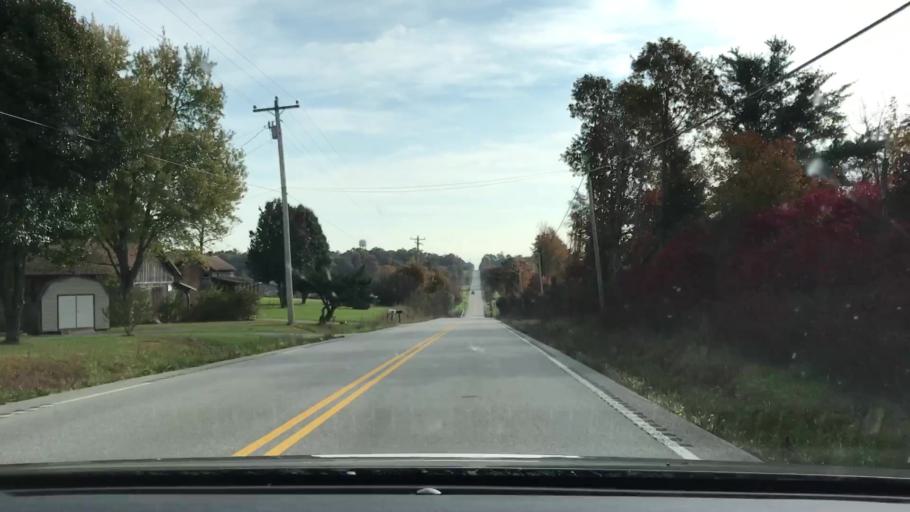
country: US
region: Tennessee
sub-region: Fentress County
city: Jamestown
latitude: 36.3818
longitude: -84.8969
